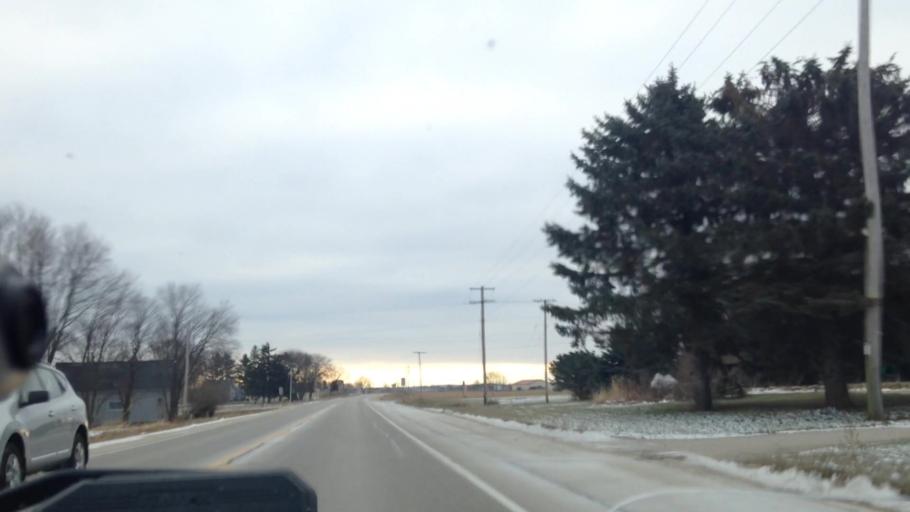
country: US
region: Wisconsin
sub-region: Dodge County
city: Theresa
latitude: 43.4250
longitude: -88.4222
